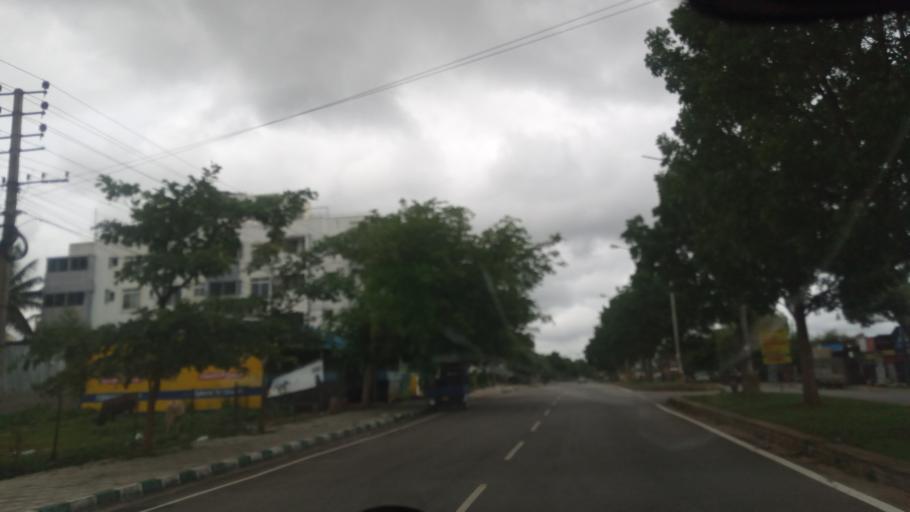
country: IN
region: Karnataka
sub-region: Mysore
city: Mysore
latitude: 12.2861
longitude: 76.6138
